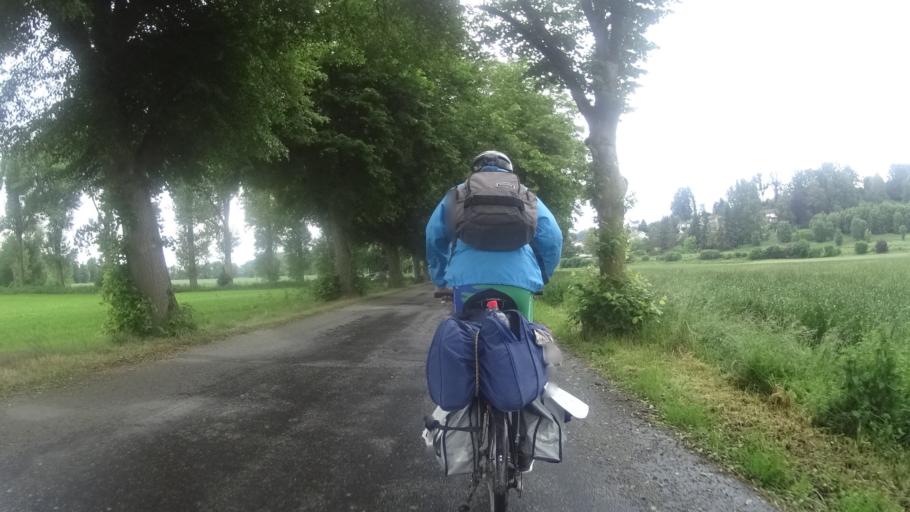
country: DE
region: Bavaria
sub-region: Lower Bavaria
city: Pfarrkirchen
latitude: 48.4341
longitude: 12.9760
